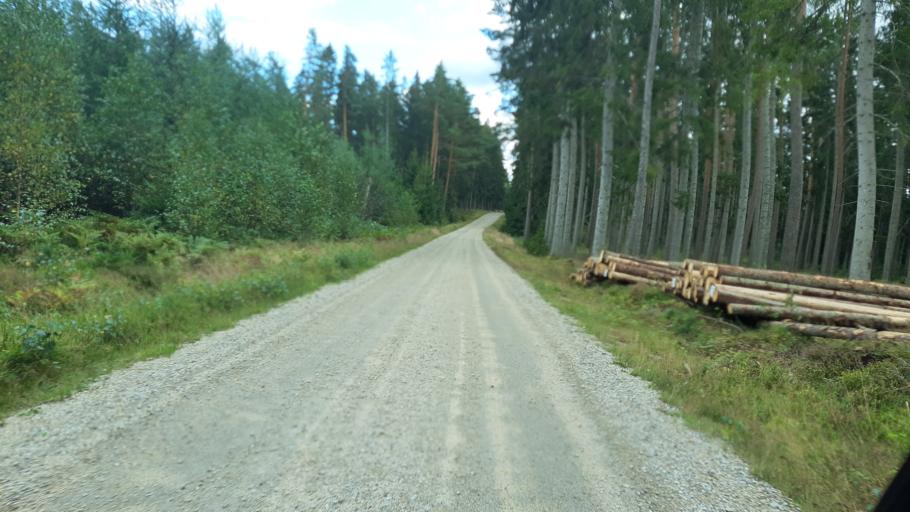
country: SE
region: Kronoberg
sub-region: Tingsryds Kommun
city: Tingsryd
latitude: 56.4401
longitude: 15.1732
